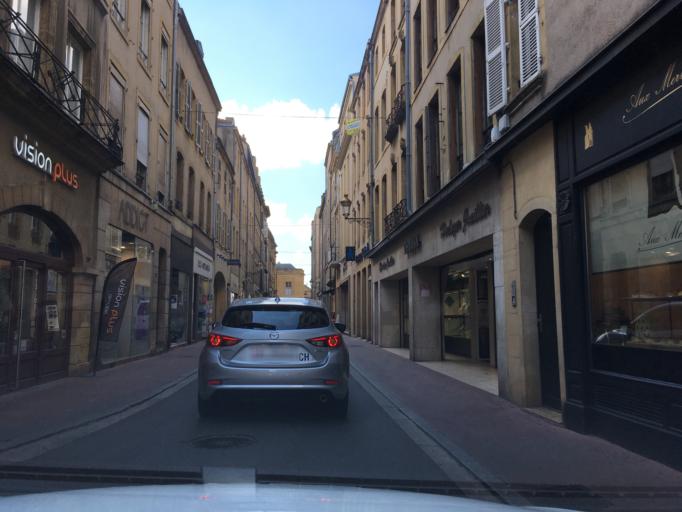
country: FR
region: Lorraine
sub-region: Departement de la Moselle
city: Metz
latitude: 49.1187
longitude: 6.1770
